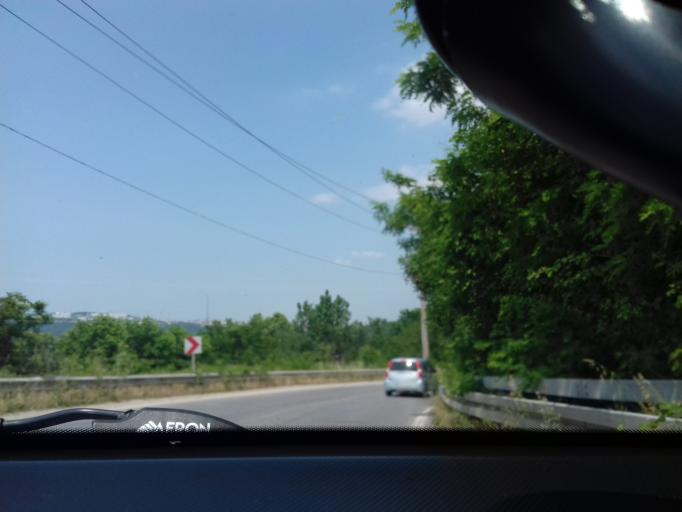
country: TR
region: Sakarya
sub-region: Merkez
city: Sapanca
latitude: 40.7051
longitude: 30.3135
